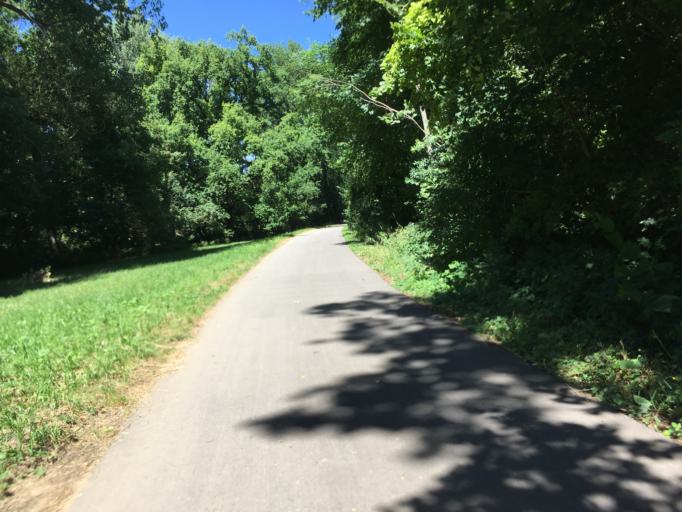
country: DE
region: Baden-Wuerttemberg
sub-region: Karlsruhe Region
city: Illingen
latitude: 48.9395
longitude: 8.9037
